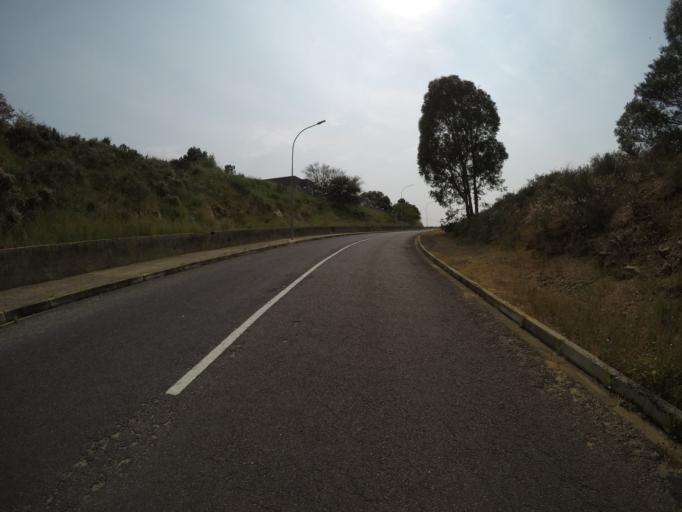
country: ZA
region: Western Cape
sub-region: West Coast District Municipality
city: Malmesbury
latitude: -33.4615
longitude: 18.7420
